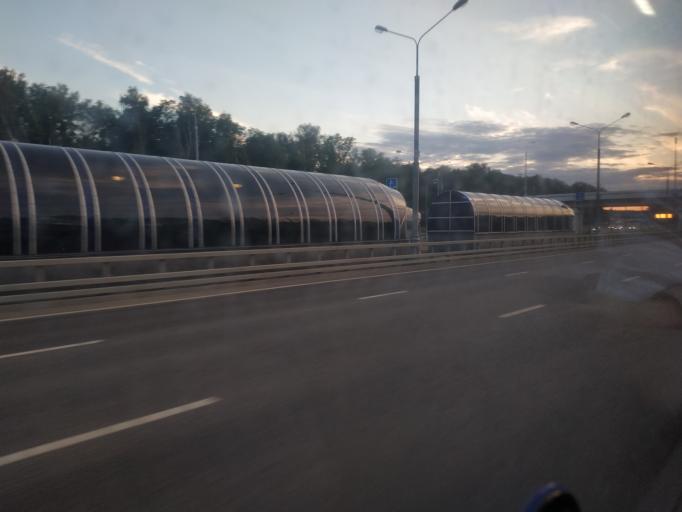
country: RU
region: Moscow
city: Solntsevo
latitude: 55.6083
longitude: 37.3953
